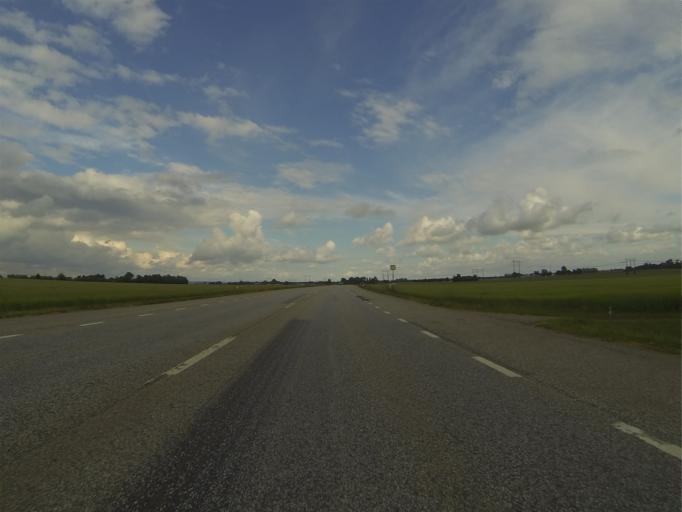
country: SE
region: Skane
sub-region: Staffanstorps Kommun
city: Hjaerup
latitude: 55.6418
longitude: 13.1559
